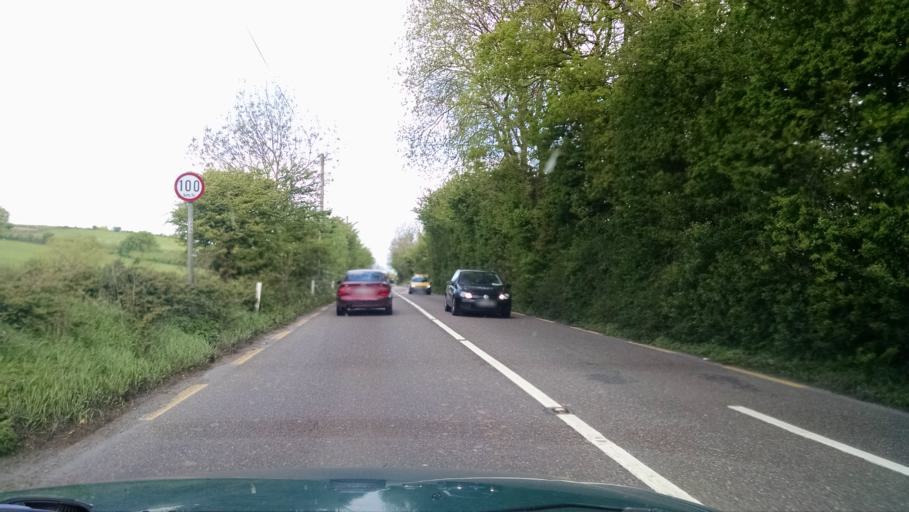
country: IE
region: Munster
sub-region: County Cork
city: Carrigaline
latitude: 51.8527
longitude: -8.4185
